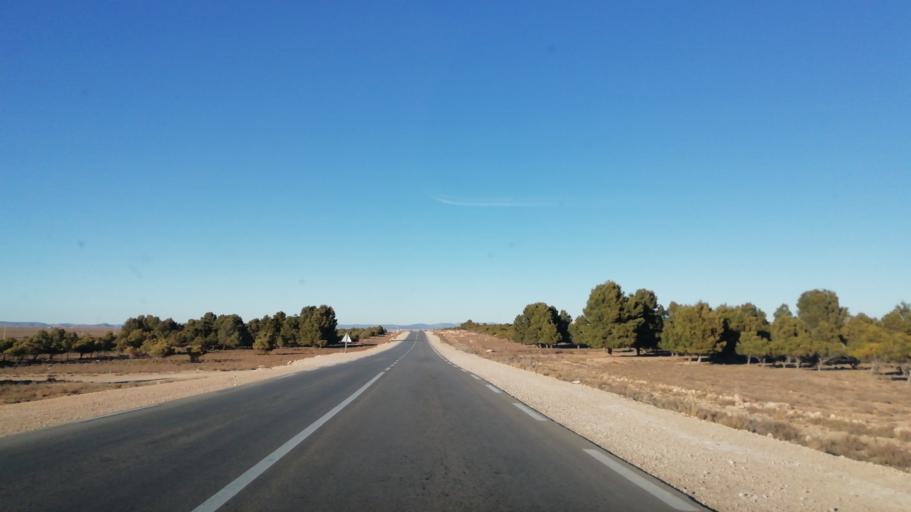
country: DZ
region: Tlemcen
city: Sebdou
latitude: 34.4409
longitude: -1.2762
